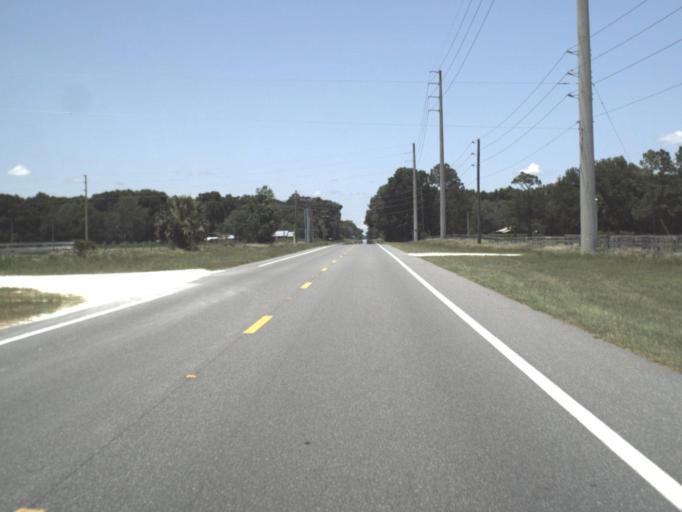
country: US
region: Florida
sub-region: Dixie County
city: Cross City
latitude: 29.7007
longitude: -82.9844
